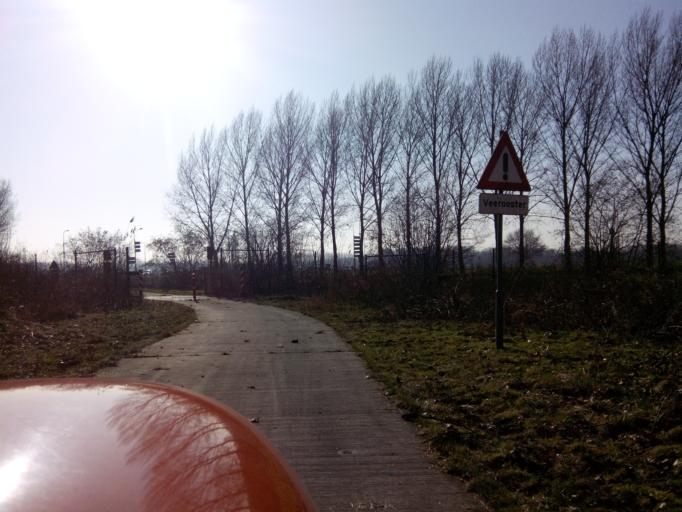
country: NL
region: Gelderland
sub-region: Gemeente Nijkerk
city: Nijkerk
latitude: 52.2827
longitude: 5.4631
